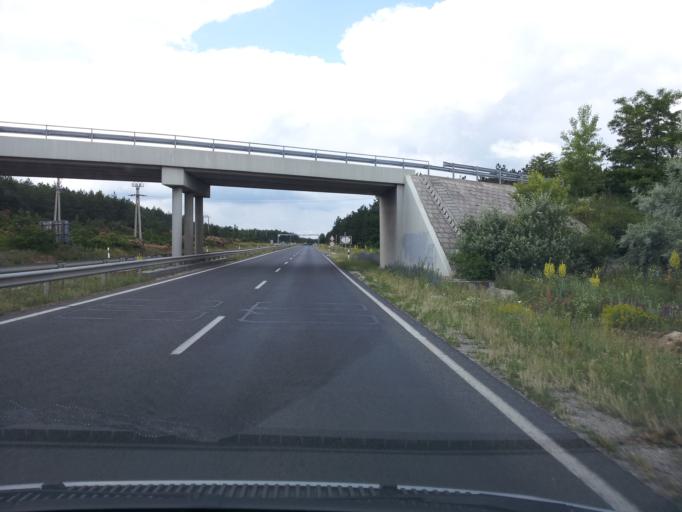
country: HU
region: Veszprem
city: Veszprem
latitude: 47.1129
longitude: 17.8531
